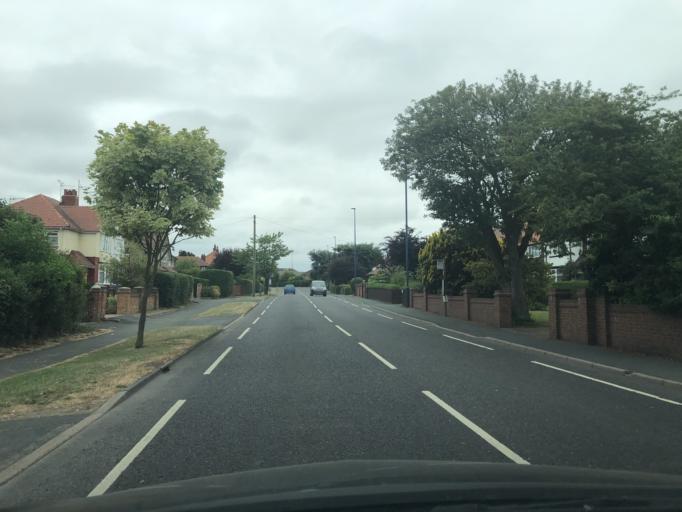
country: GB
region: England
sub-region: North Yorkshire
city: Filey
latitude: 54.2072
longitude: -0.2996
